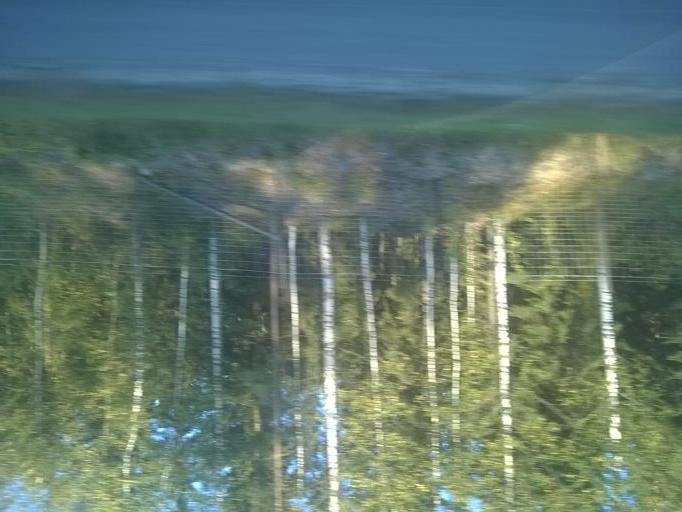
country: FI
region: Pirkanmaa
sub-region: Tampere
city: Tampere
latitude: 61.4266
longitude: 23.7546
